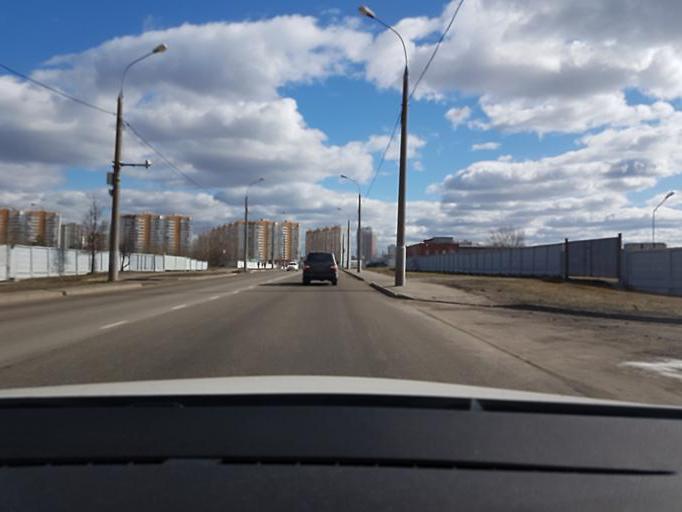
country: RU
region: Moskovskaya
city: Pavshino
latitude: 55.8373
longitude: 37.3440
